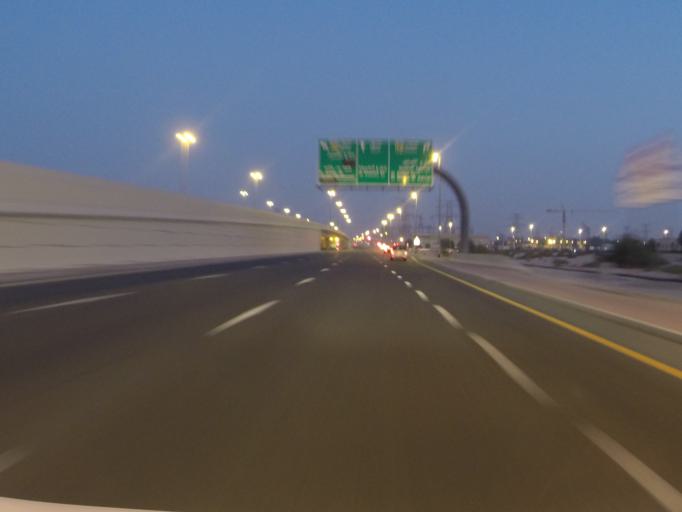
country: AE
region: Dubai
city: Dubai
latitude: 25.0696
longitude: 55.1908
